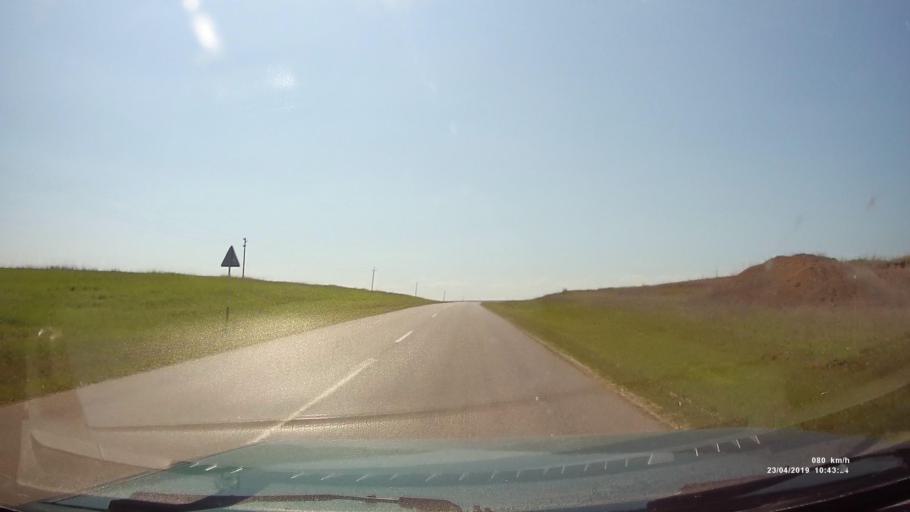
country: RU
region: Kalmykiya
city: Yashalta
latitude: 46.4706
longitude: 42.6497
